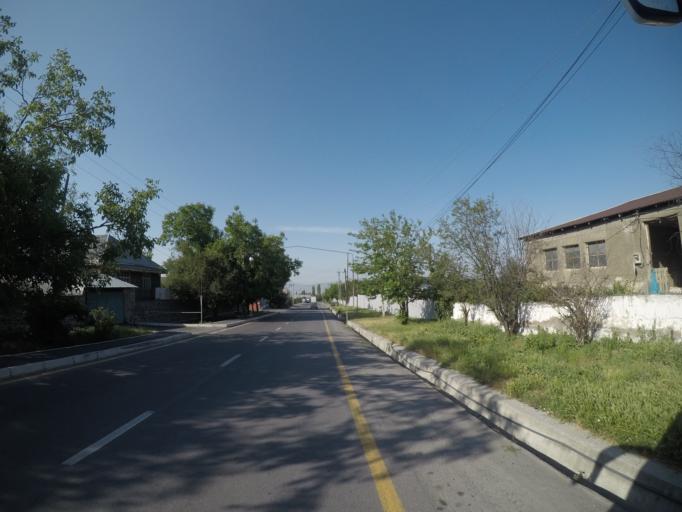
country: AZ
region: Shaki City
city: Sheki
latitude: 41.2146
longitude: 47.1679
